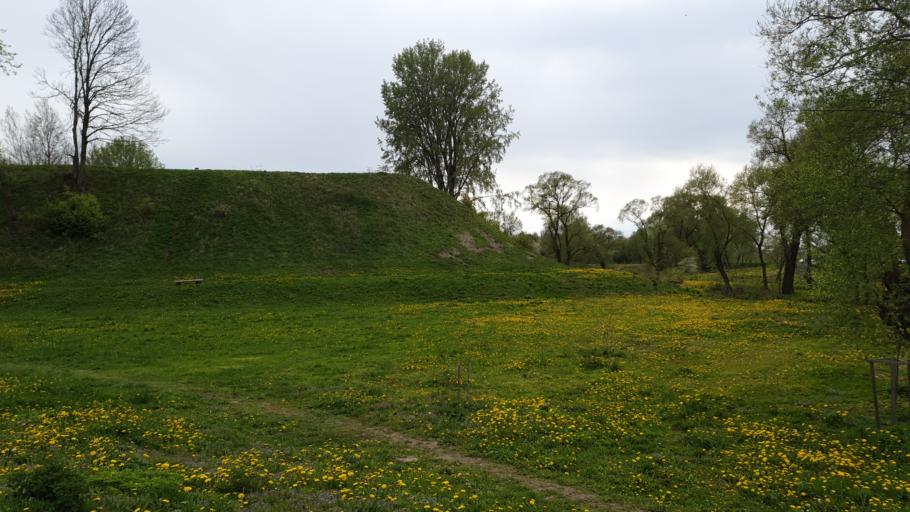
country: BY
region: Minsk
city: Azyartso
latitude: 53.8295
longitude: 27.3373
